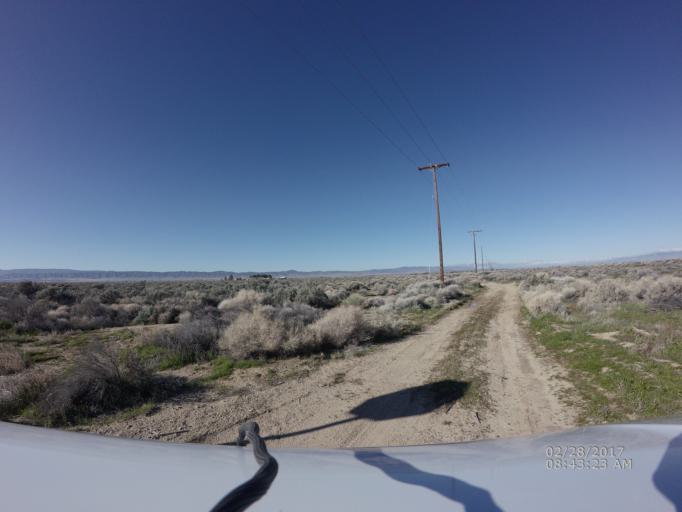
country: US
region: California
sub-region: Los Angeles County
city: Quartz Hill
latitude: 34.7621
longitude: -118.2373
